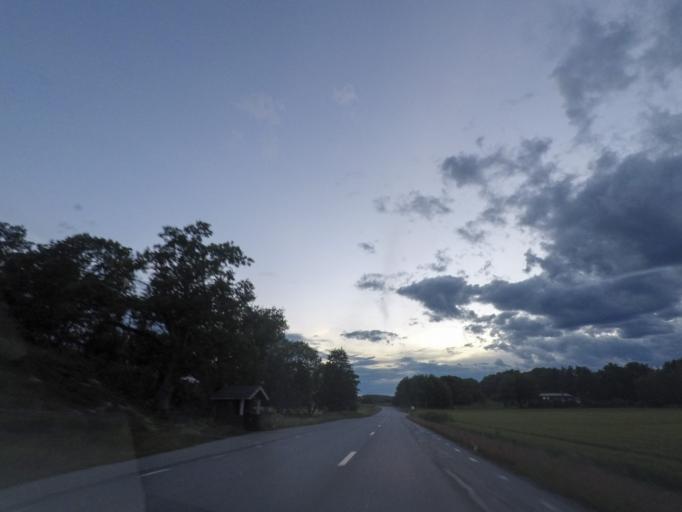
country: SE
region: Uppsala
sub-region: Enkopings Kommun
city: Dalby
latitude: 59.6522
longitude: 17.4108
